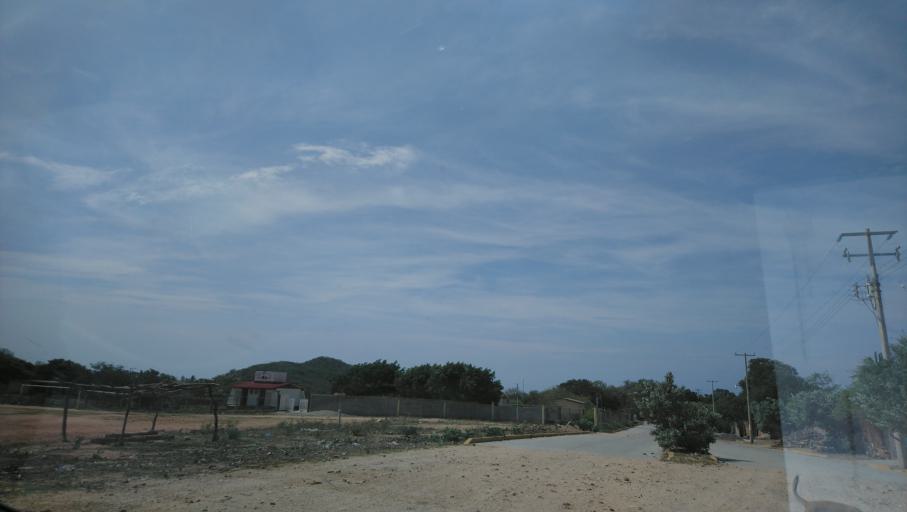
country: MX
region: Oaxaca
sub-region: Salina Cruz
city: Salina Cruz
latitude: 16.2133
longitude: -95.1251
